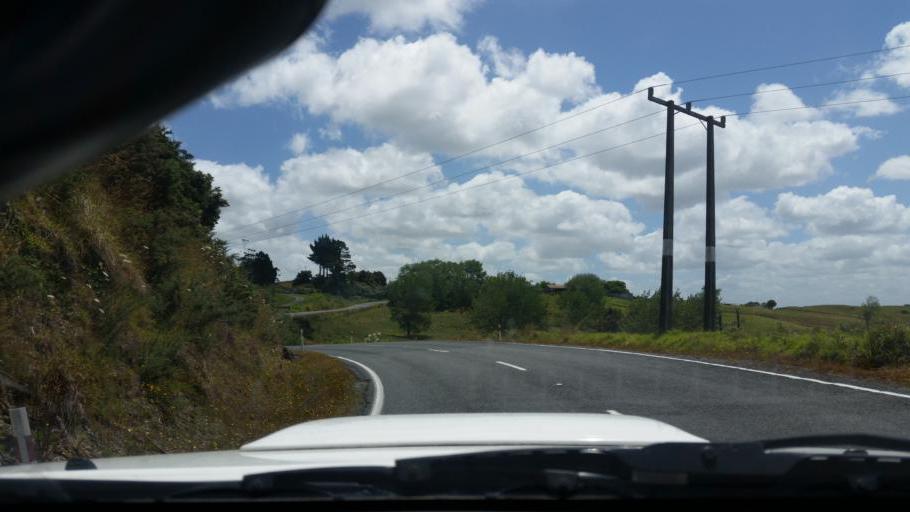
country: NZ
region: Northland
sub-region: Whangarei
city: Ruakaka
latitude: -36.0779
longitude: 174.2492
